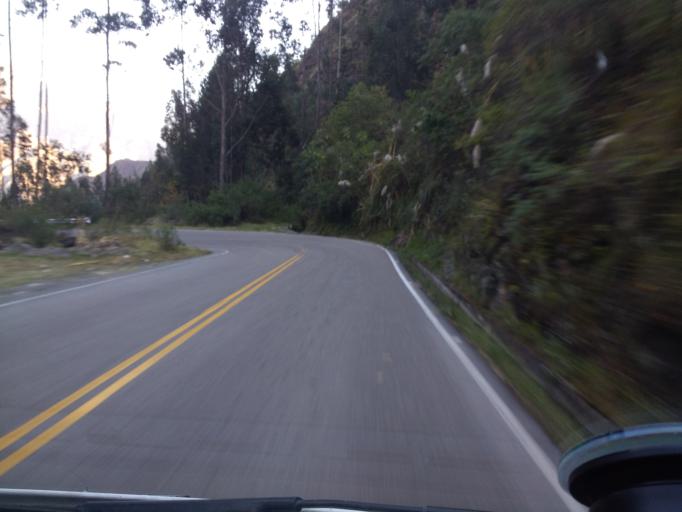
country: PE
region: Cusco
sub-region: Provincia de Urubamba
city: Ollantaytambo
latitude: -13.2016
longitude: -72.2965
